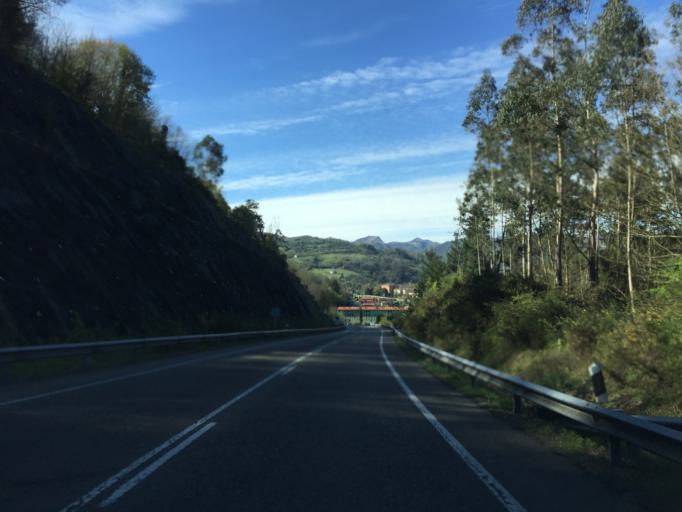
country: ES
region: Asturias
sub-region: Province of Asturias
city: Castandiello
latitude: 43.3590
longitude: -5.9585
